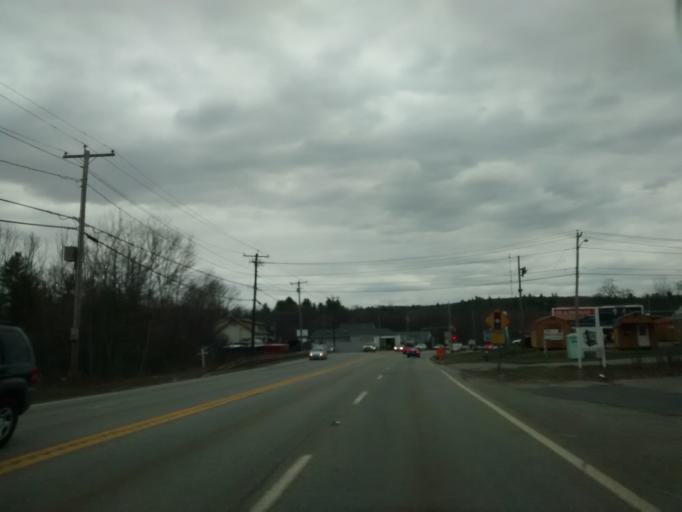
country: US
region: Massachusetts
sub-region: Worcester County
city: Oxford
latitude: 42.1661
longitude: -71.8959
